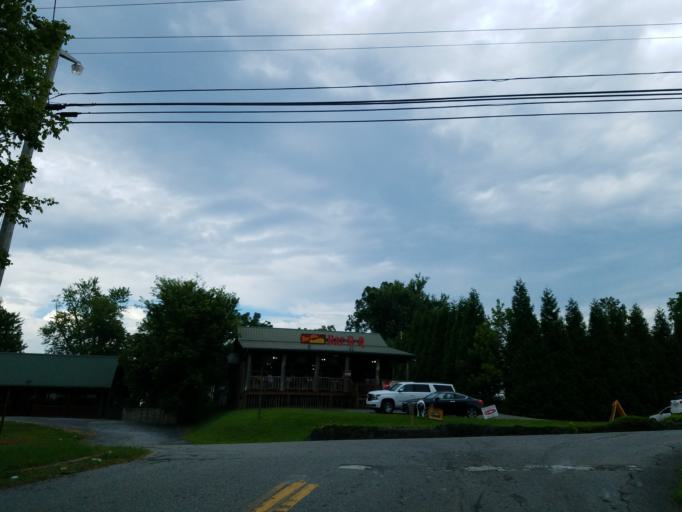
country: US
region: Georgia
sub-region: Fannin County
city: Blue Ridge
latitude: 34.8722
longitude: -84.3163
